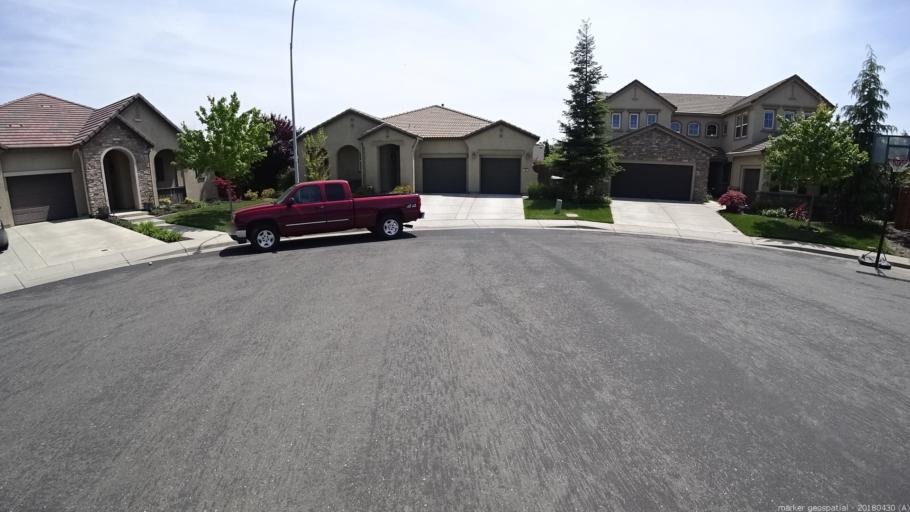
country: US
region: California
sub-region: Yolo County
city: West Sacramento
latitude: 38.5432
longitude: -121.5341
